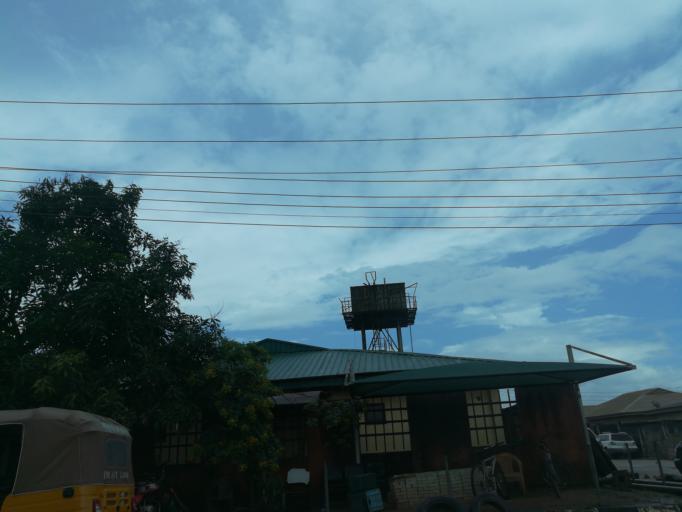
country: NG
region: Lagos
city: Ikorodu
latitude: 6.6356
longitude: 3.5128
